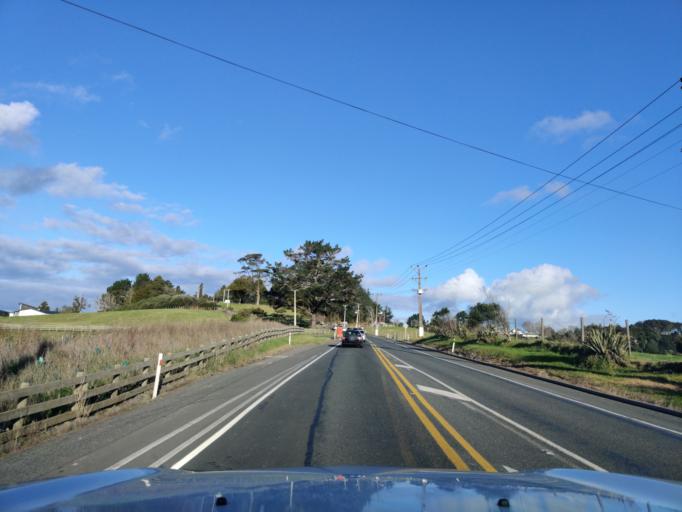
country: NZ
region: Auckland
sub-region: Auckland
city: Red Hill
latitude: -36.9667
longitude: 174.9834
